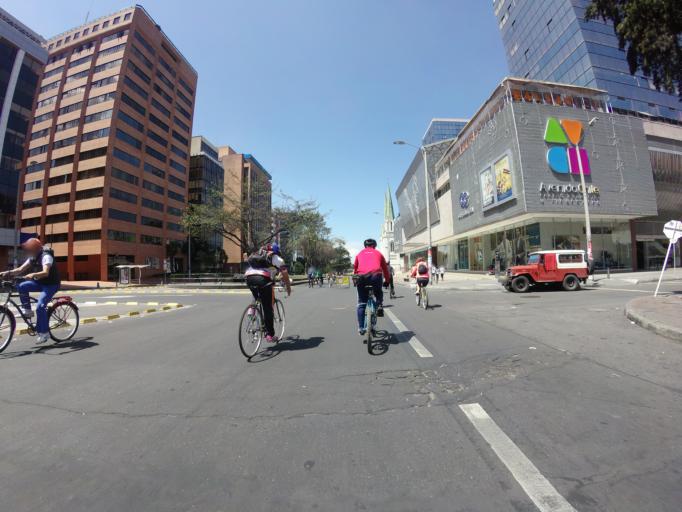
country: CO
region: Bogota D.C.
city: Barrio San Luis
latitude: 4.6567
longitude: -74.0575
